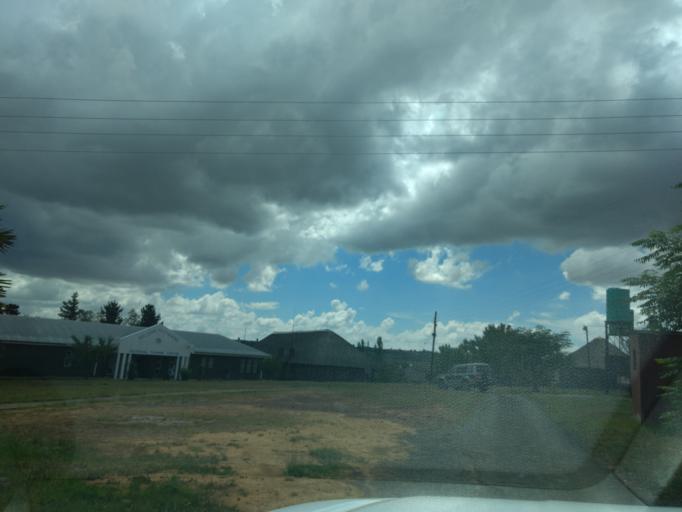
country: LS
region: Maseru
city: Maseru
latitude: -29.3958
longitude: 27.5534
